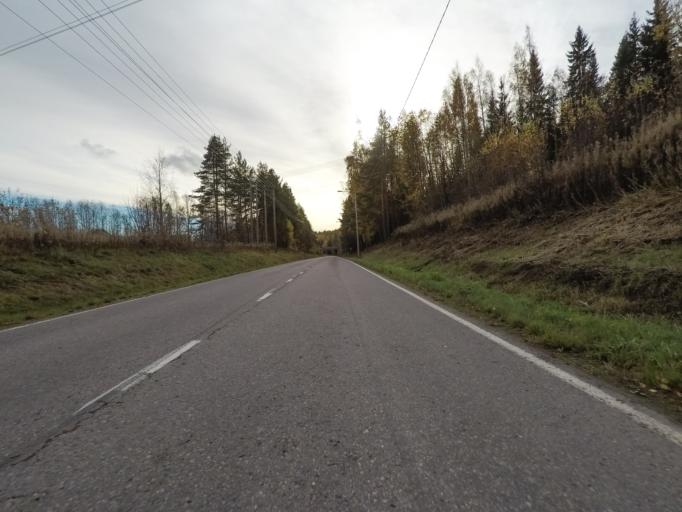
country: FI
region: Uusimaa
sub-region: Helsinki
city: Vantaa
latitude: 60.2629
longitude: 25.1409
